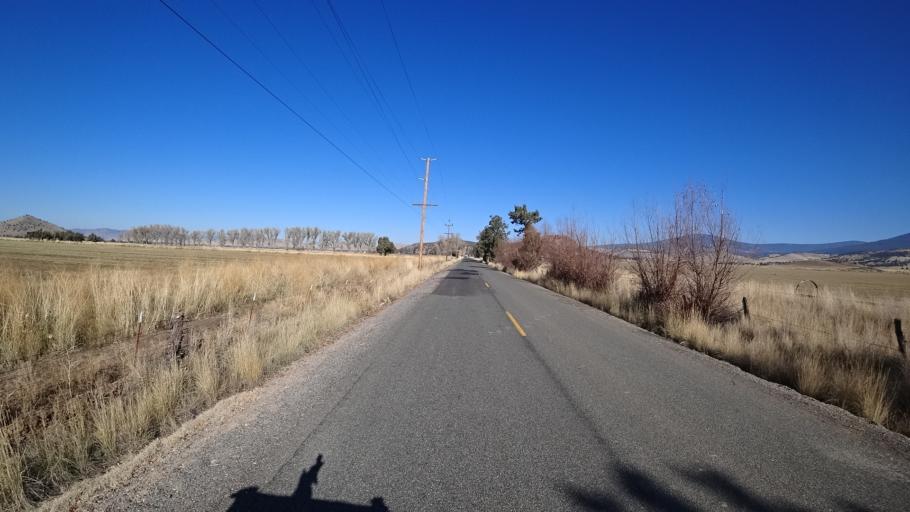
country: US
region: California
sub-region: Siskiyou County
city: Montague
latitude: 41.6800
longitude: -122.3698
